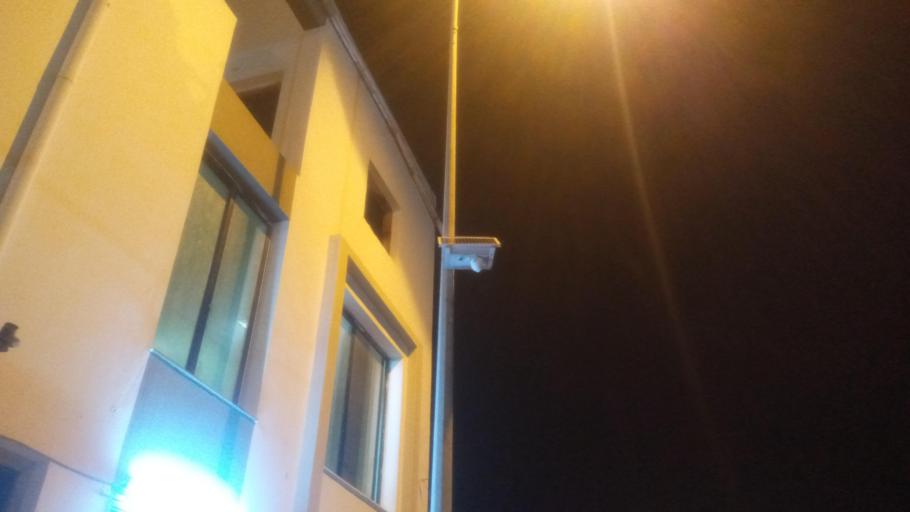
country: TN
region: Madanin
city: Bin Qirdan
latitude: 33.1385
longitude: 11.2210
